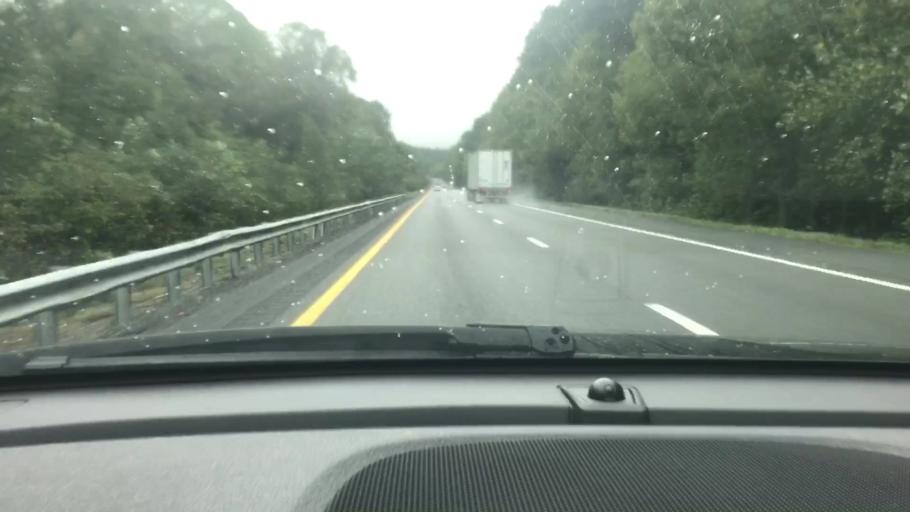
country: US
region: Tennessee
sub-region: Cheatham County
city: Pegram
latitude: 36.0847
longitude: -87.0484
